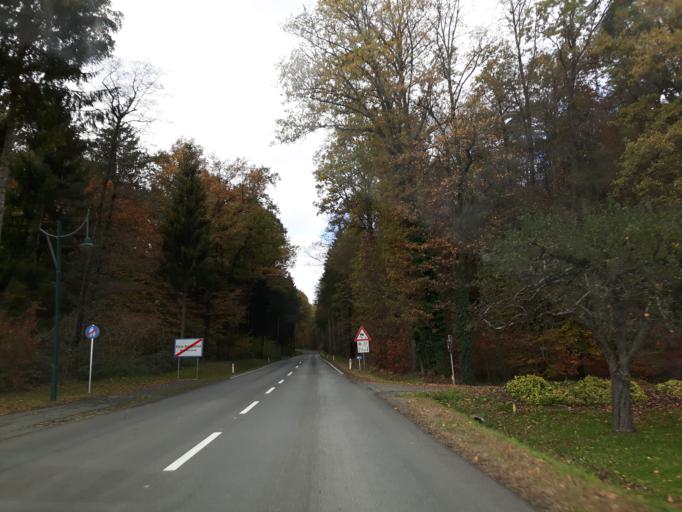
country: AT
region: Styria
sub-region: Politischer Bezirk Leibnitz
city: Breitenfeld am Tannenriegel
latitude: 46.8422
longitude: 15.6288
